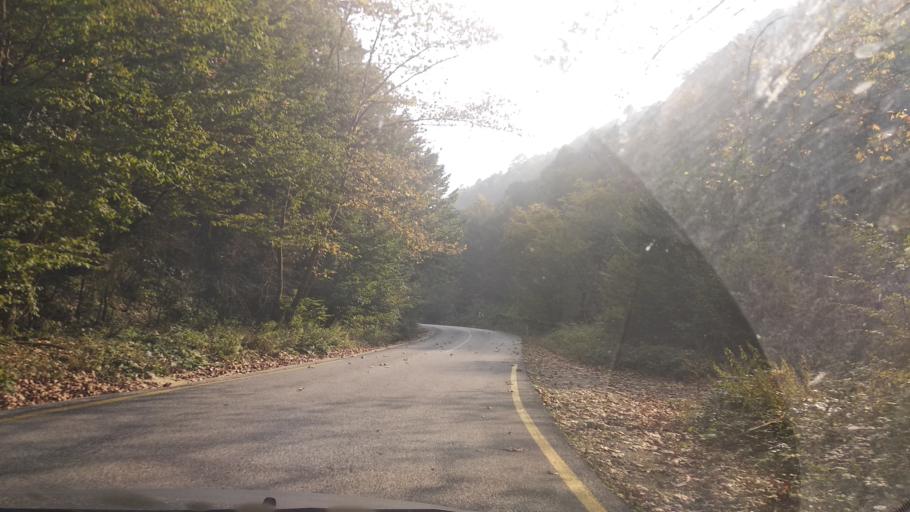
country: TR
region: Duzce
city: Kaynasli
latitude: 40.7209
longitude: 31.2628
